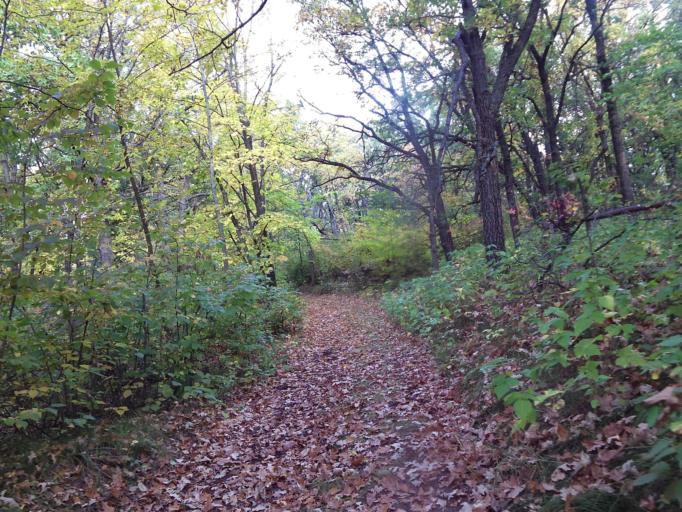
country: US
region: North Dakota
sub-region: Pembina County
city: Cavalier
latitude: 48.7792
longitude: -97.7318
